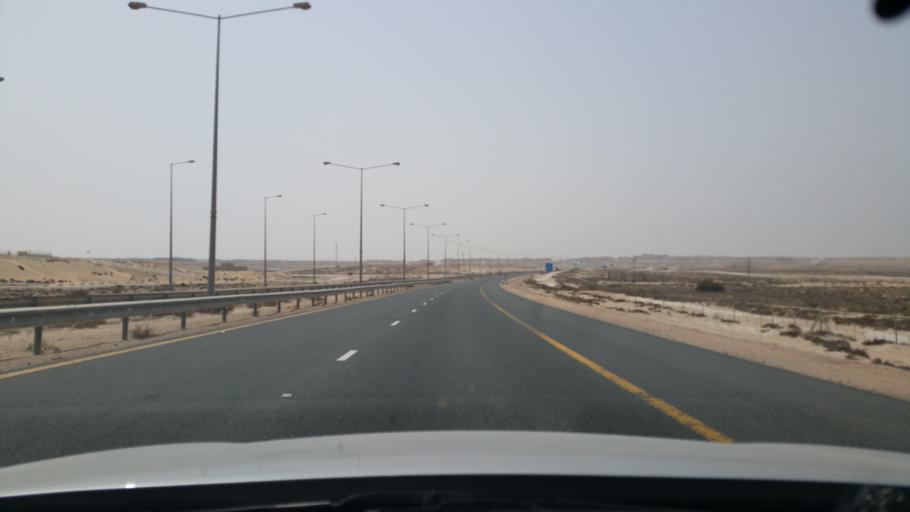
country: QA
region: Baladiyat ar Rayyan
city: Dukhan
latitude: 25.3488
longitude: 50.7819
